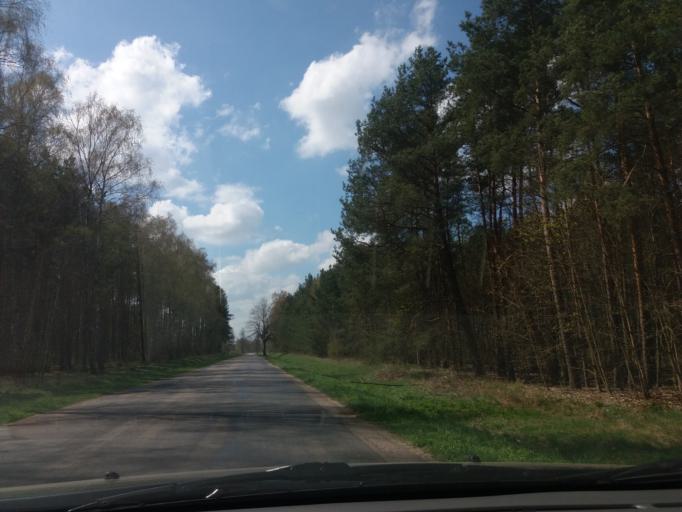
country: PL
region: Warmian-Masurian Voivodeship
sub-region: Powiat szczycienski
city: Jedwabno
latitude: 53.3594
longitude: 20.6823
